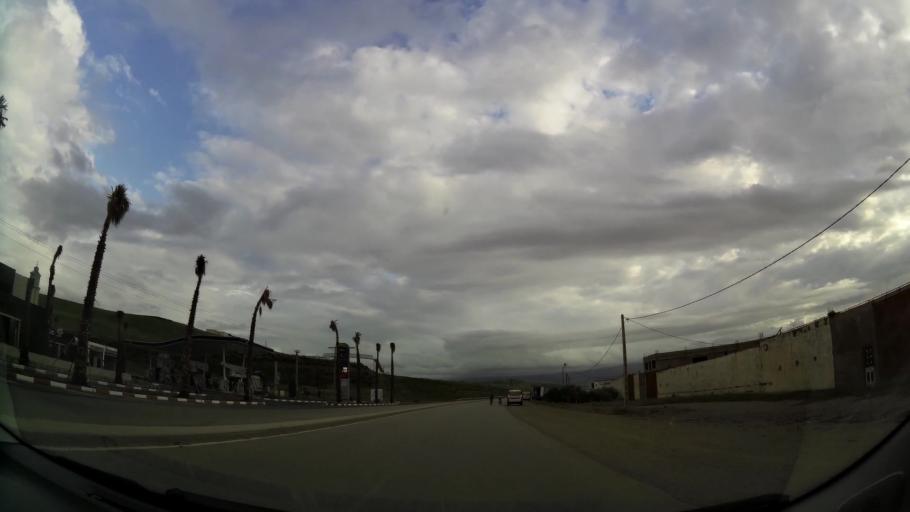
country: MA
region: Taza-Al Hoceima-Taounate
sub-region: Taza
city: Taza
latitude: 34.2665
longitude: -3.9573
